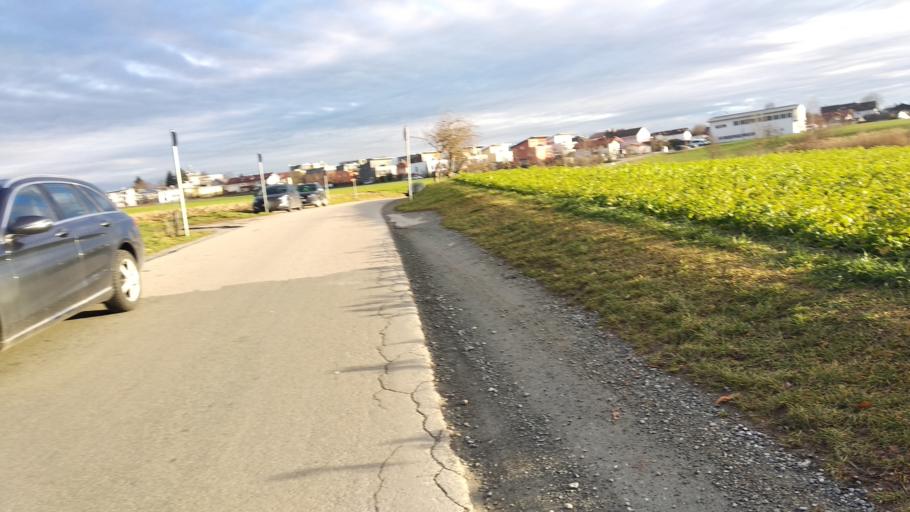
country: DE
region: Bavaria
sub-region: Upper Bavaria
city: Ebersberg
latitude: 48.0786
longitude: 11.9504
